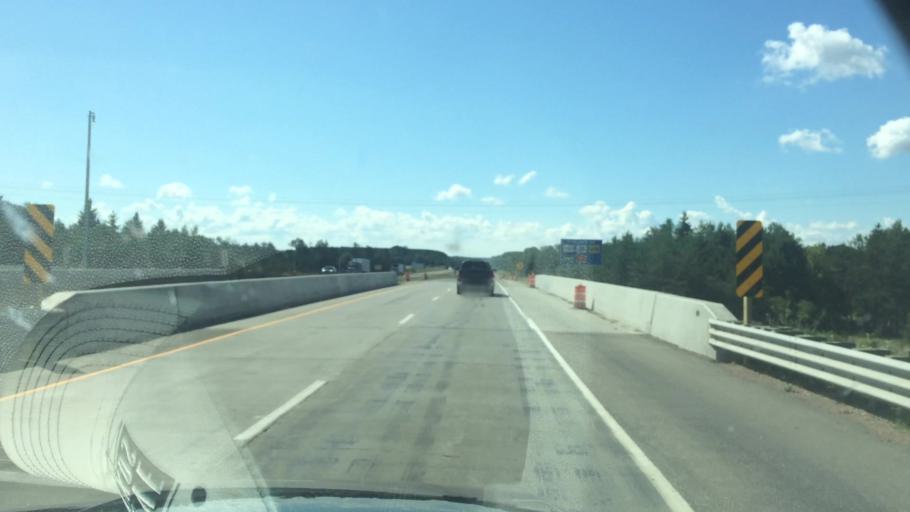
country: US
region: Wisconsin
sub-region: Portage County
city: Stevens Point
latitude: 44.5410
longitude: -89.5449
